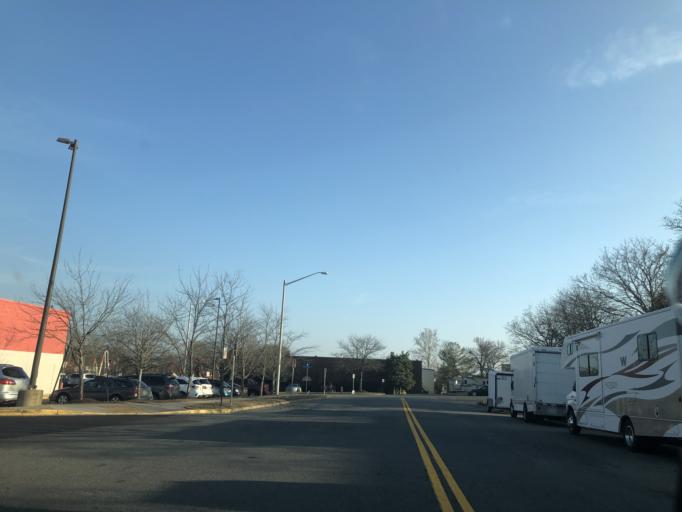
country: US
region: Virginia
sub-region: Fairfax County
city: Floris
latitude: 38.9332
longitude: -77.4232
